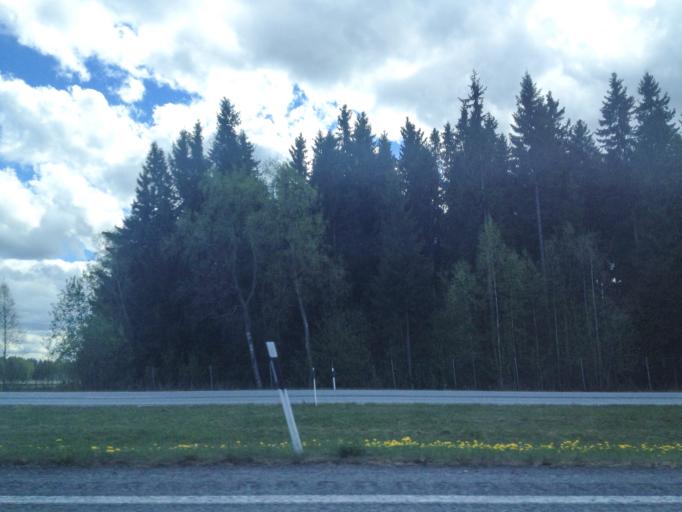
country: FI
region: Haeme
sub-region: Haemeenlinna
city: Parola
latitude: 61.0796
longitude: 24.2461
